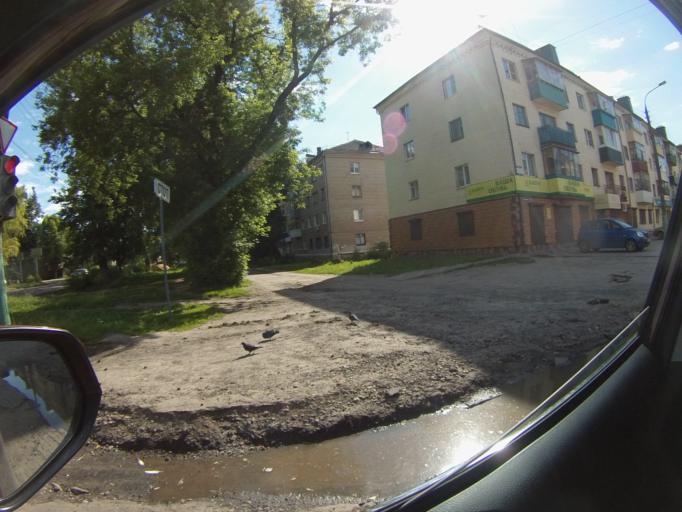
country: RU
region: Orjol
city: Mtsensk
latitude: 53.2764
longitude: 36.5772
